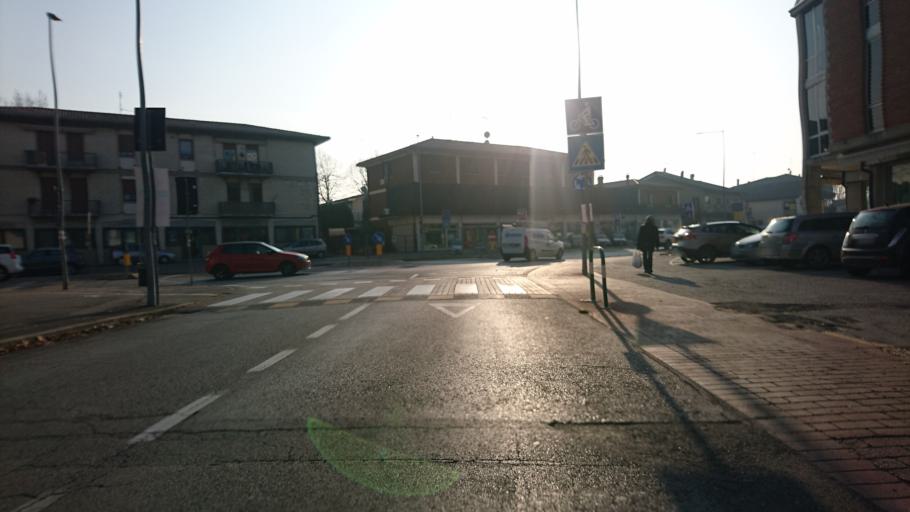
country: IT
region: Veneto
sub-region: Provincia di Padova
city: Tencarola
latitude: 45.3961
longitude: 11.8275
